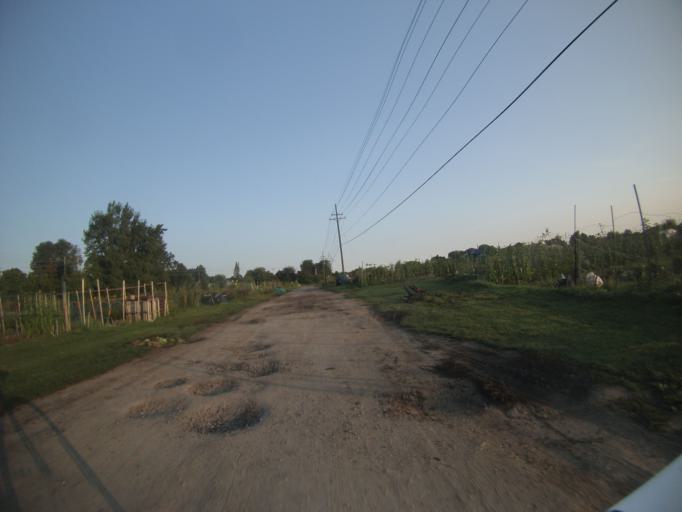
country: CA
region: Ontario
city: Ottawa
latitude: 45.3893
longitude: -75.6385
